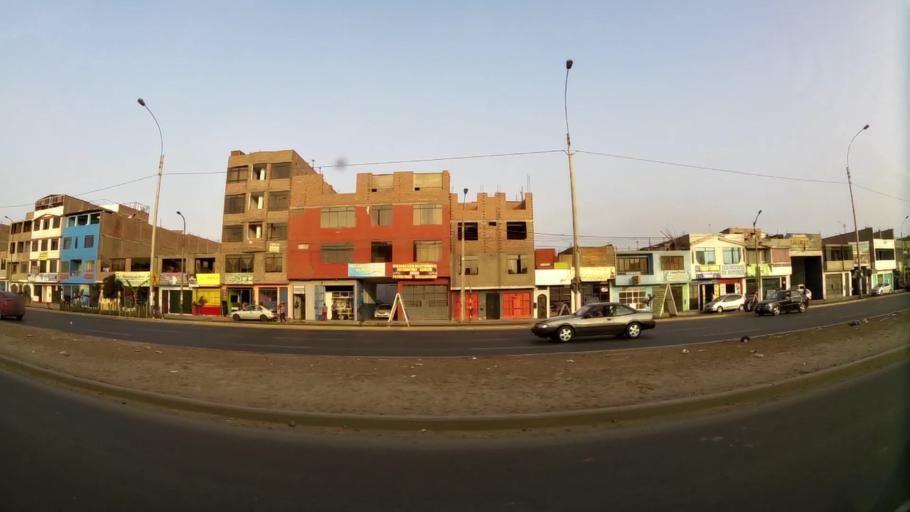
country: PE
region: Callao
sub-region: Callao
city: Callao
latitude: -11.9934
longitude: -77.1097
